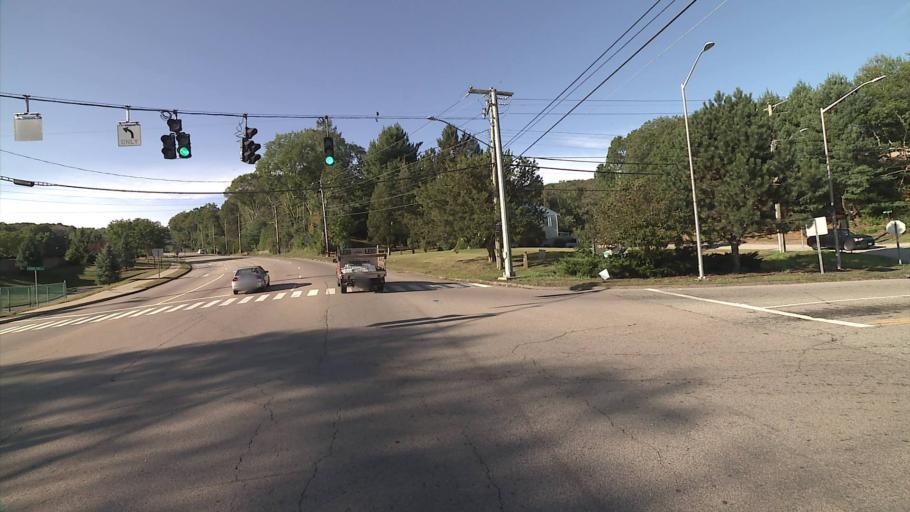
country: US
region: Connecticut
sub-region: New London County
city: Norwich
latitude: 41.4947
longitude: -72.1001
